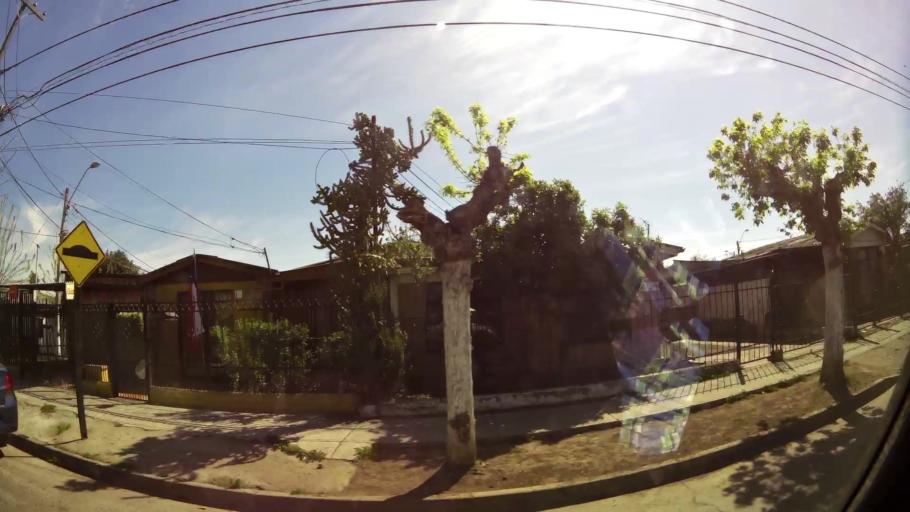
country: CL
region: Santiago Metropolitan
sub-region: Provincia de Santiago
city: Lo Prado
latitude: -33.5027
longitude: -70.7241
